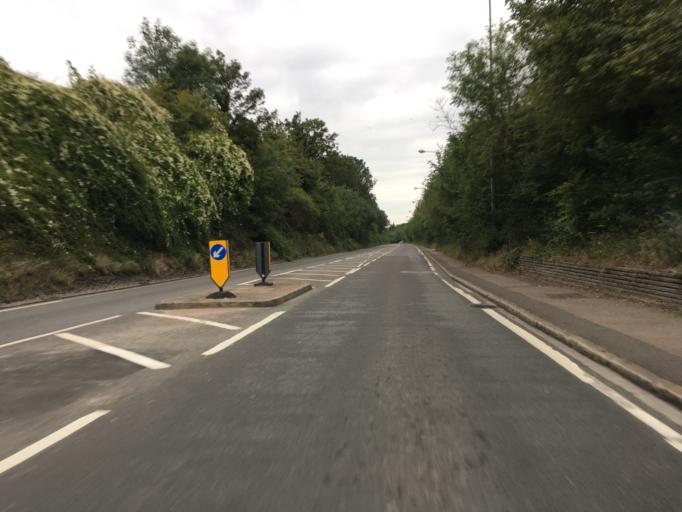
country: GB
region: England
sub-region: Central Bedfordshire
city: Houghton Regis
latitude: 51.8975
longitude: -0.5370
